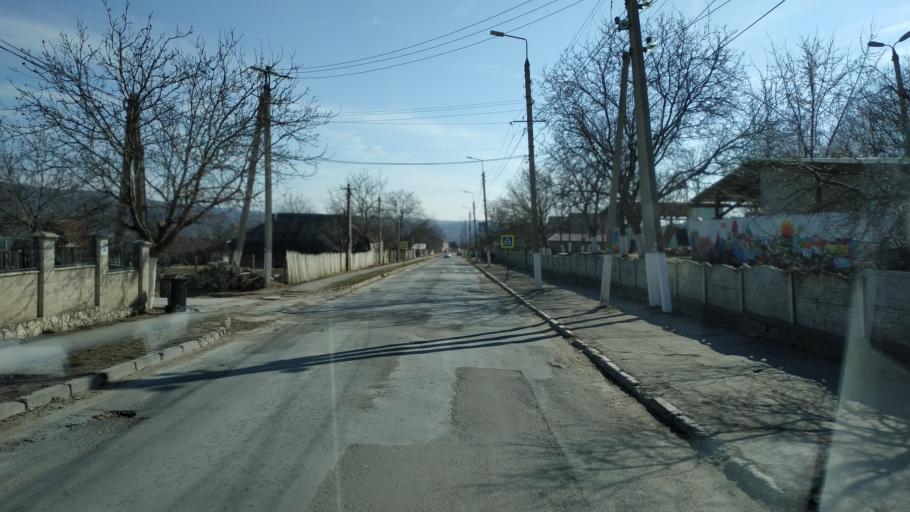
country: MD
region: Nisporeni
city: Nisporeni
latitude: 47.0787
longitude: 28.1678
